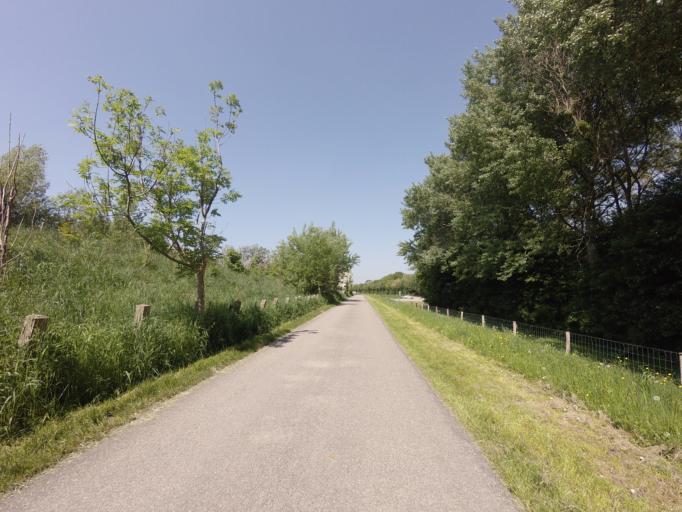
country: NL
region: Zeeland
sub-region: Gemeente Veere
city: Veere
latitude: 51.5325
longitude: 3.6777
